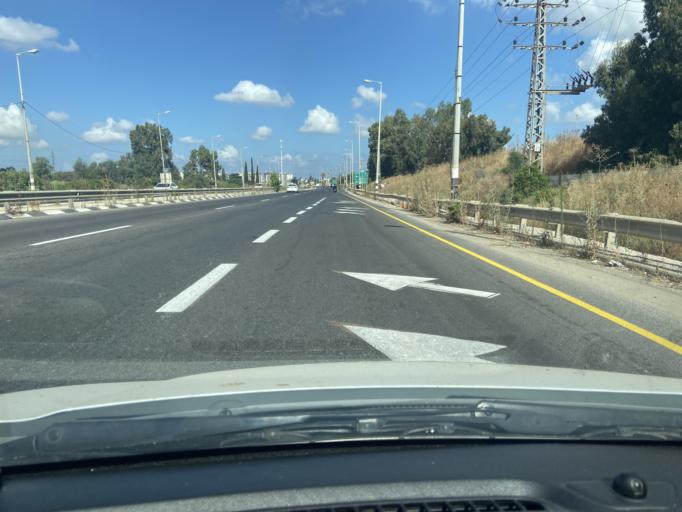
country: IL
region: Central District
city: Yehud
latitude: 32.0258
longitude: 34.8970
